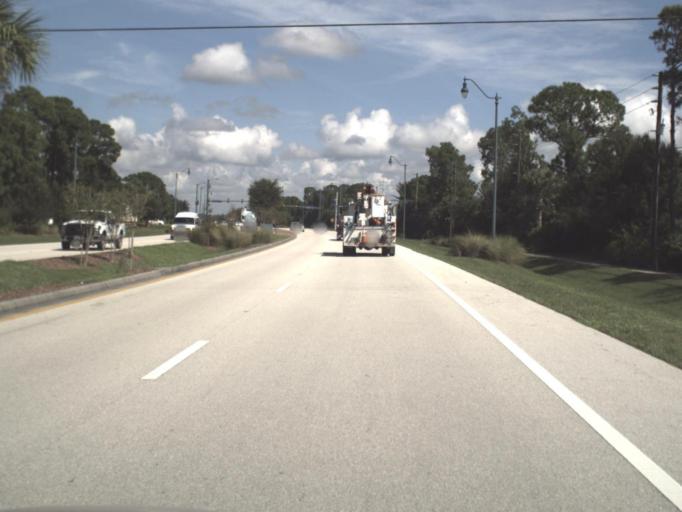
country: US
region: Florida
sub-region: Sarasota County
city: North Port
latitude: 27.0498
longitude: -82.1573
